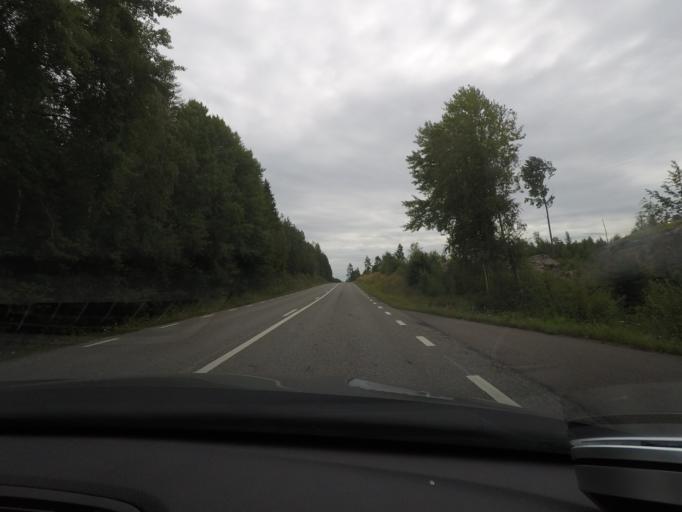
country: SE
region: Blekinge
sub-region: Olofstroms Kommun
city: Olofstroem
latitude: 56.4484
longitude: 14.5526
